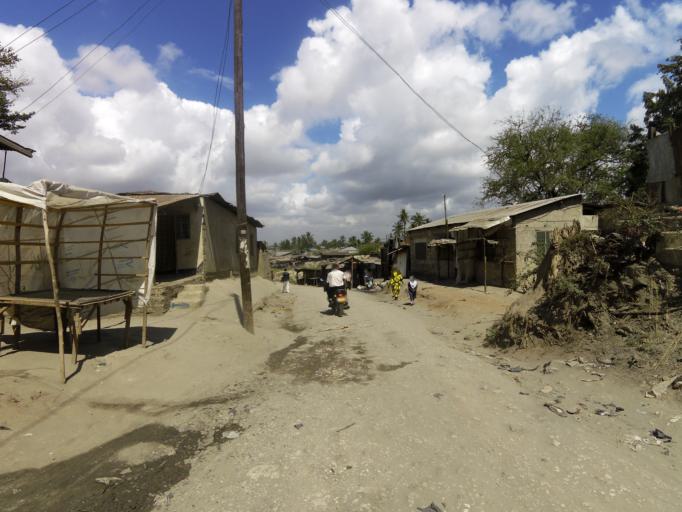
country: TZ
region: Dar es Salaam
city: Magomeni
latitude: -6.7914
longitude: 39.2479
